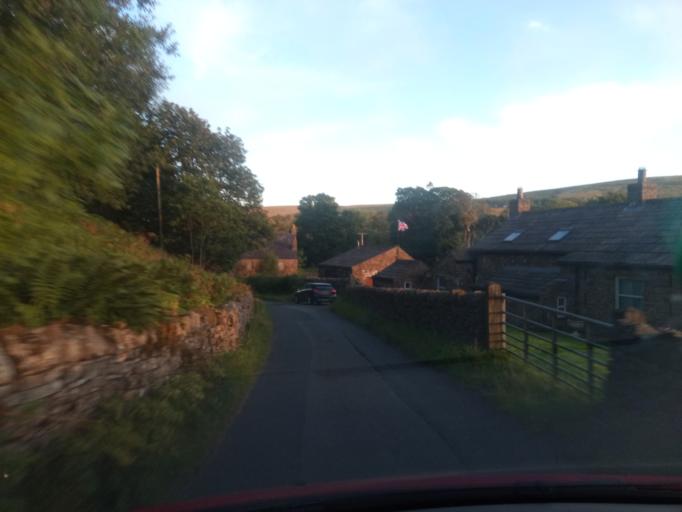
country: GB
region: England
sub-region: Northumberland
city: Bardon Mill
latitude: 54.8071
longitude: -2.3760
